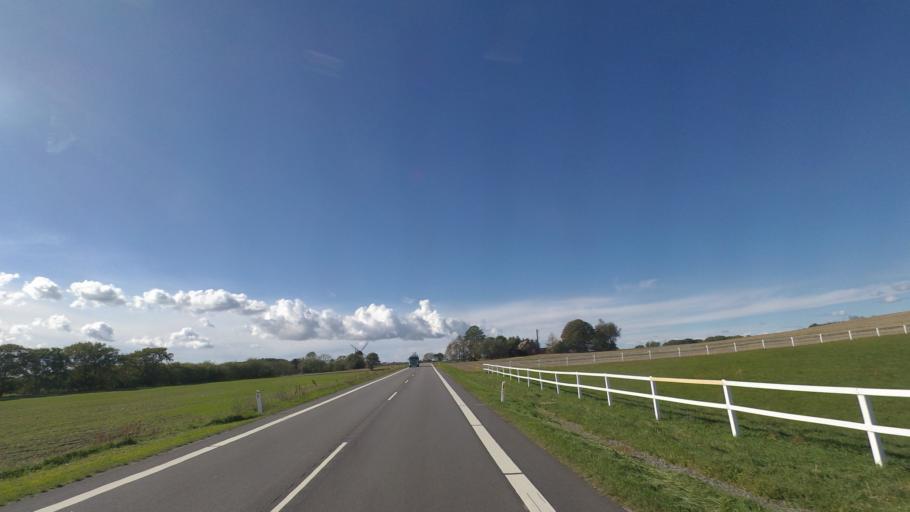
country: DK
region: Capital Region
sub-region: Bornholm Kommune
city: Akirkeby
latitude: 55.0692
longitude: 14.9704
